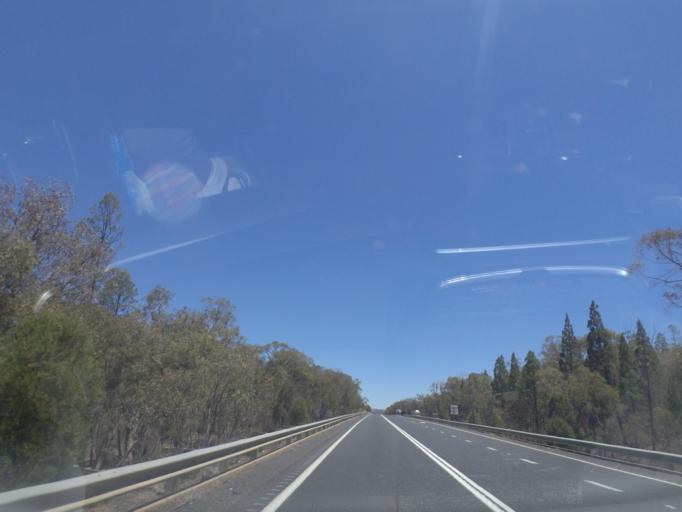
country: AU
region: New South Wales
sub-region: Warrumbungle Shire
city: Coonabarabran
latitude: -31.2310
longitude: 149.3194
